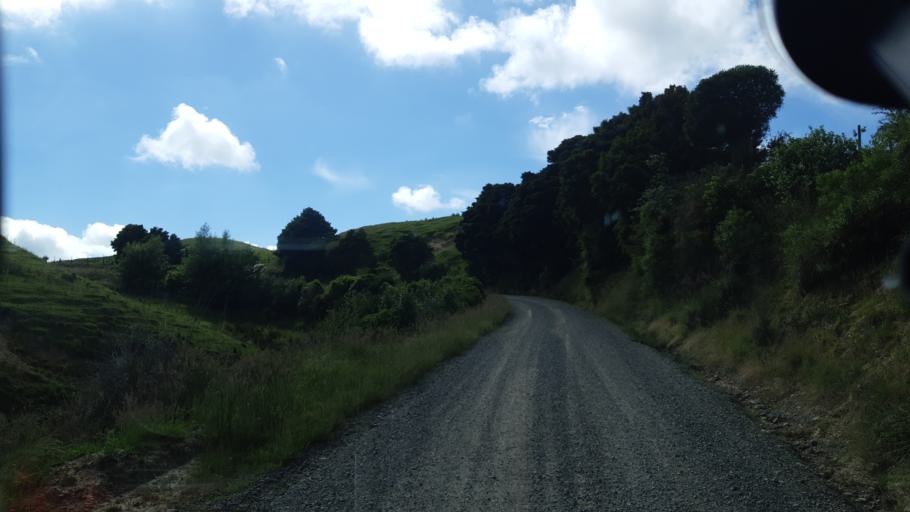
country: NZ
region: Manawatu-Wanganui
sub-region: Rangitikei District
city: Bulls
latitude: -39.9607
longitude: 175.4837
